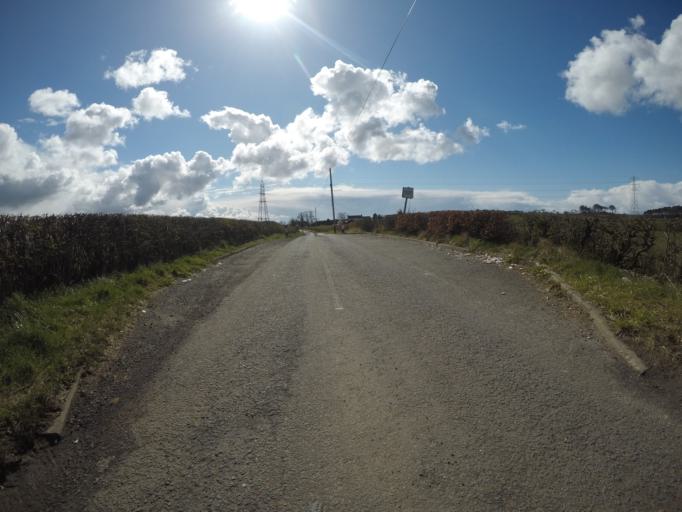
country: GB
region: Scotland
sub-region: North Ayrshire
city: Kilwinning
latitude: 55.6734
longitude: -4.7225
